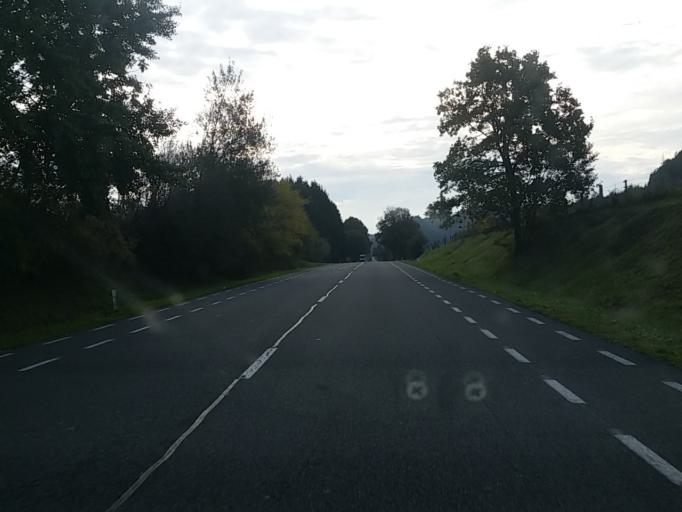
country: BE
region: Wallonia
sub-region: Province du Luxembourg
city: Herbeumont
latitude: 49.7194
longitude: 5.2474
